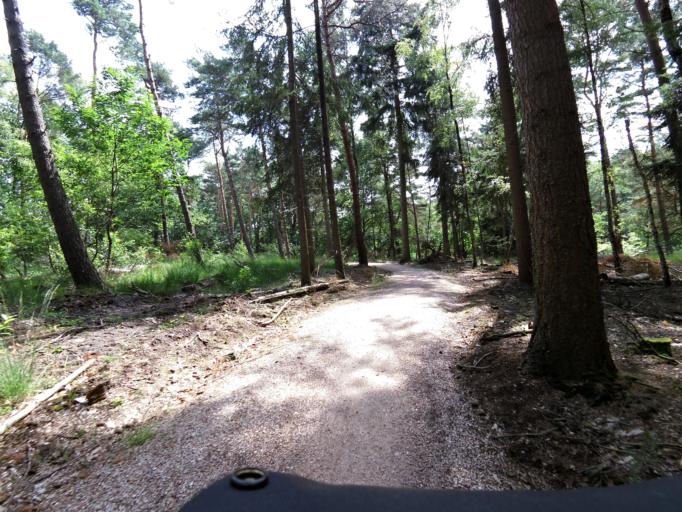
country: NL
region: Limburg
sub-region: Gemeente Roerdalen
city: Vlodrop
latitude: 51.1601
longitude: 6.1027
